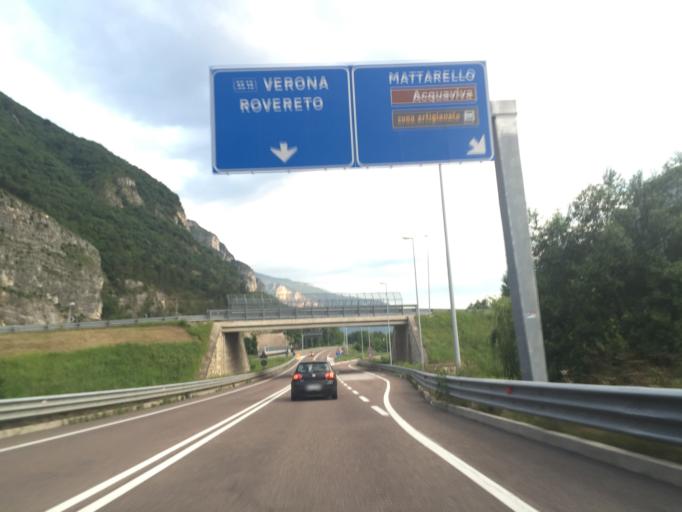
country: IT
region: Trentino-Alto Adige
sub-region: Provincia di Trento
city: Aldeno
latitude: 45.9803
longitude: 11.1152
